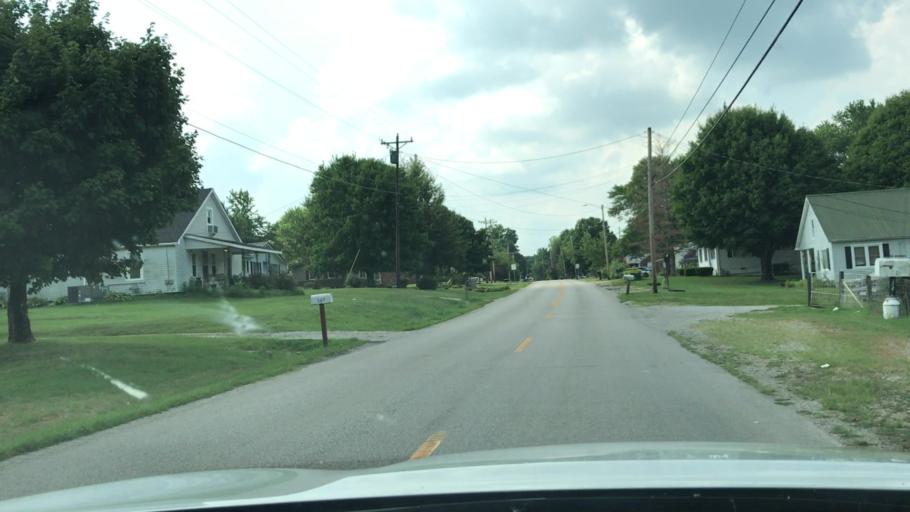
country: US
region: Kentucky
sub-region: Todd County
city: Elkton
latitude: 36.8048
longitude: -87.1484
